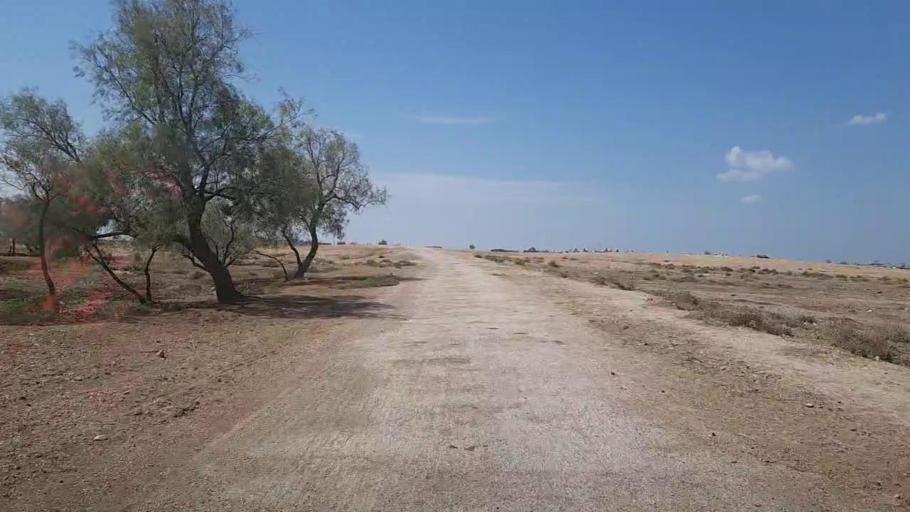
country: PK
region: Sindh
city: Sehwan
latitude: 26.3501
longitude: 67.6736
